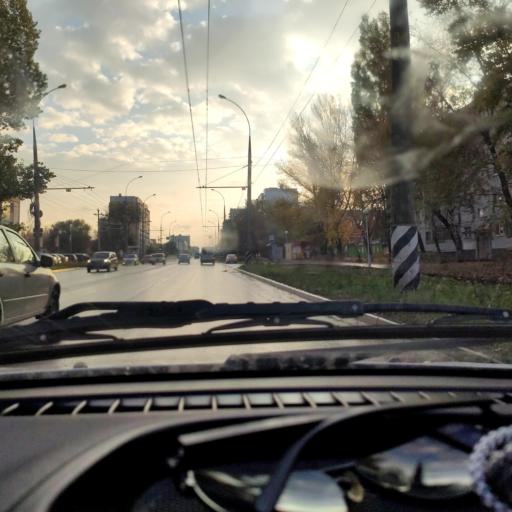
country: RU
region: Samara
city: Tol'yatti
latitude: 53.5359
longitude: 49.3021
